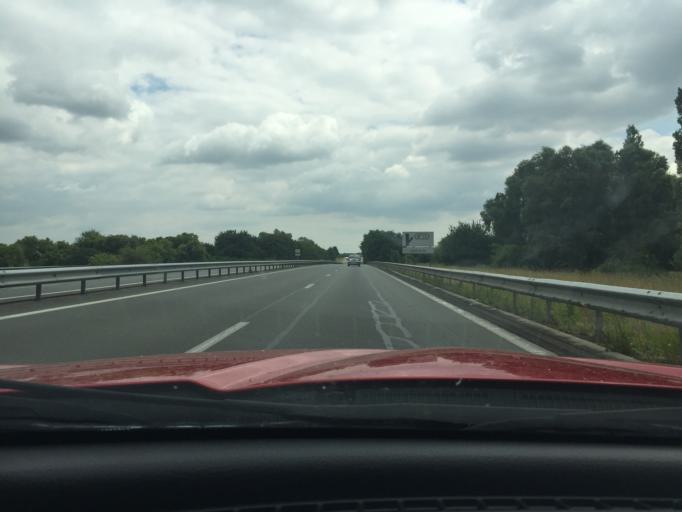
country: FR
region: Picardie
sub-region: Departement de l'Aisne
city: Aulnois-sous-Laon
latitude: 49.6217
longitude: 3.6327
